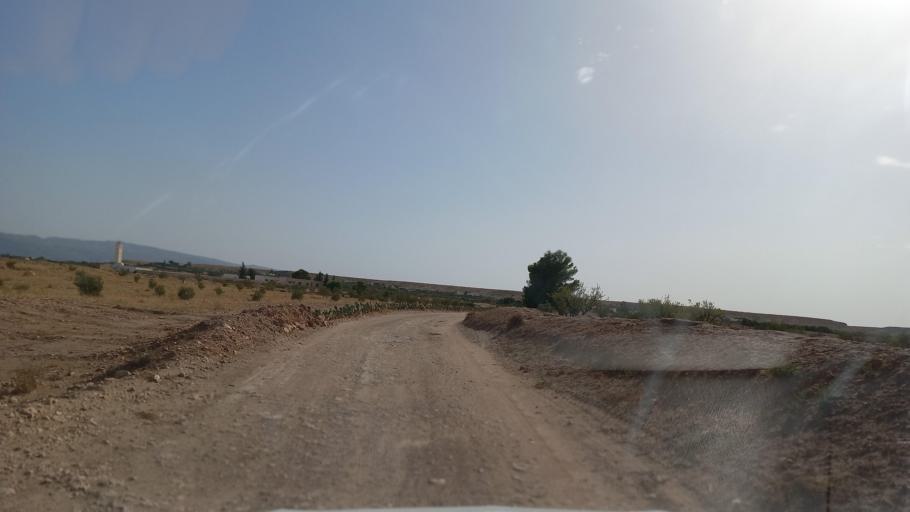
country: TN
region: Al Qasrayn
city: Kasserine
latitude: 35.2690
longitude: 8.9356
